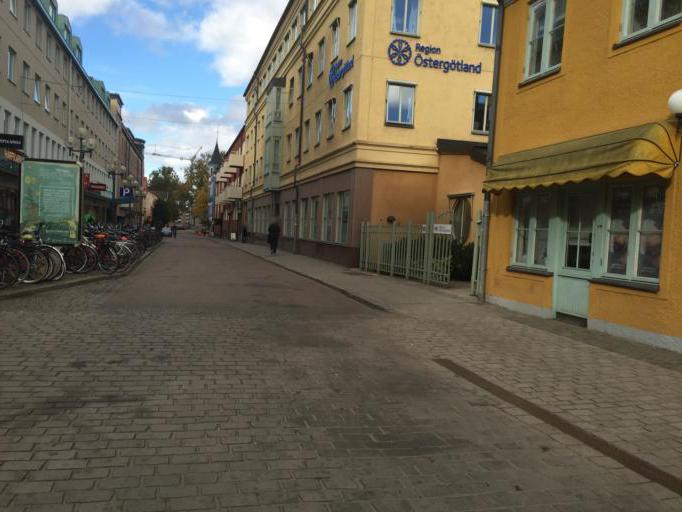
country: SE
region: OEstergoetland
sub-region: Linkopings Kommun
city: Linkoping
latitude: 58.4118
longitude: 15.6225
